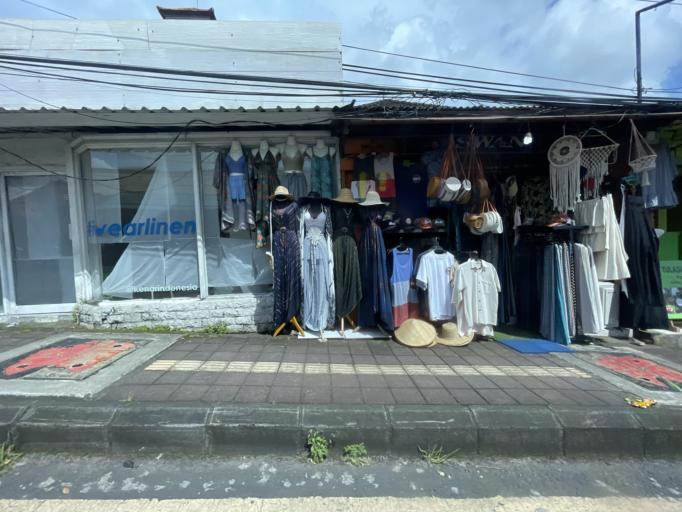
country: ID
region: Bali
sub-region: Kabupaten Gianyar
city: Ubud
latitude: -8.5167
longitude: 115.2599
